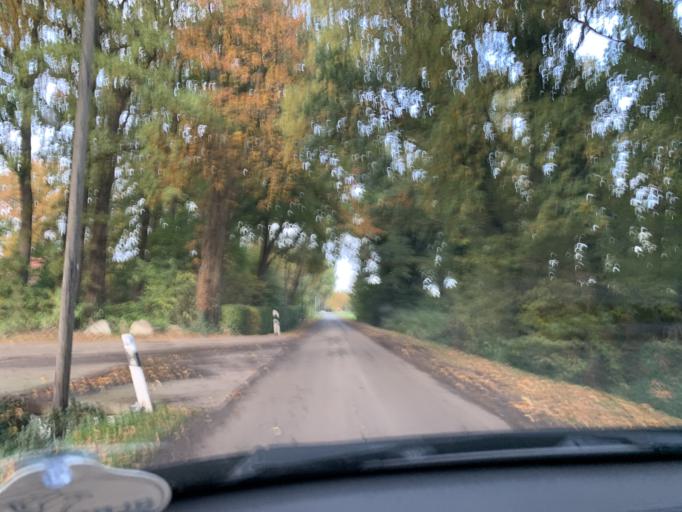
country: DE
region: Lower Saxony
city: Wiefelstede
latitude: 53.2600
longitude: 8.0968
